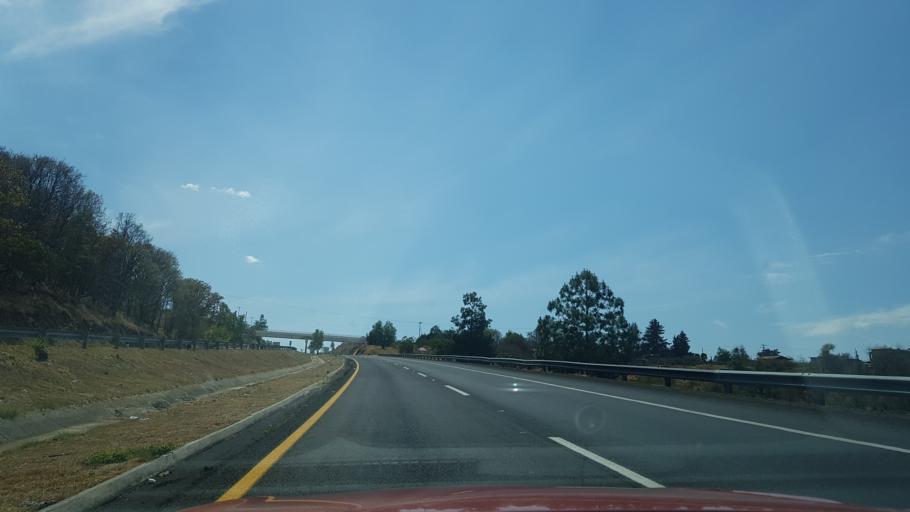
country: MX
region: Michoacan
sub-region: Maravatio
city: Santiago Puriatzicuaro
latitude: 19.9036
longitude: -100.5769
